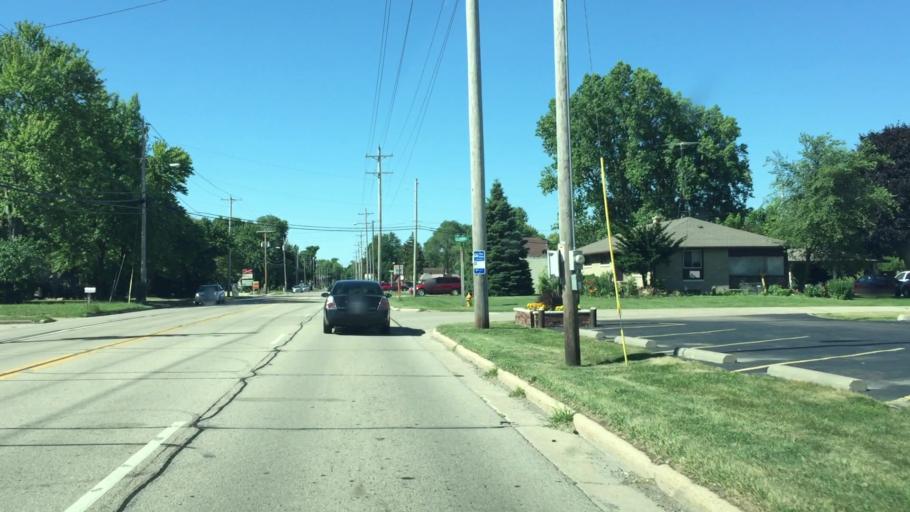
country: US
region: Wisconsin
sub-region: Winnebago County
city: Menasha
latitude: 44.2198
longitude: -88.4298
